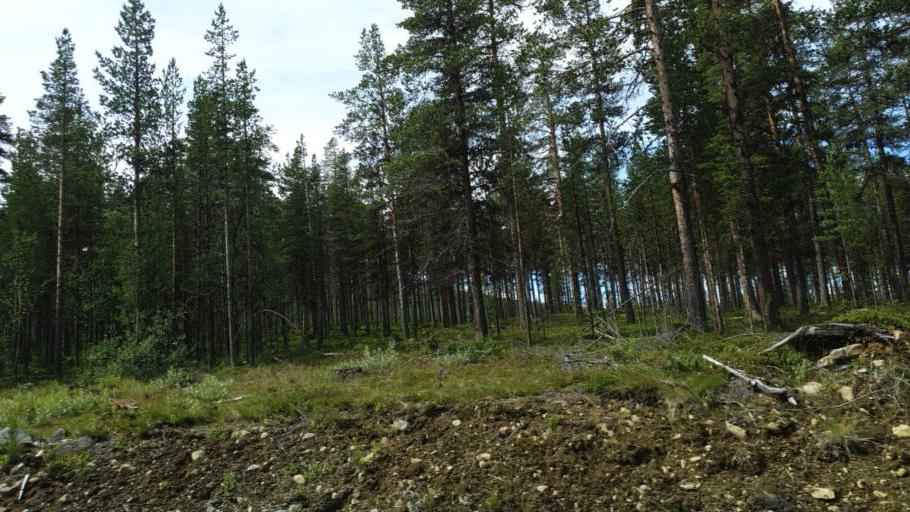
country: NO
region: Oppland
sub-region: Vaga
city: Vagamo
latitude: 61.7075
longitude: 9.0574
